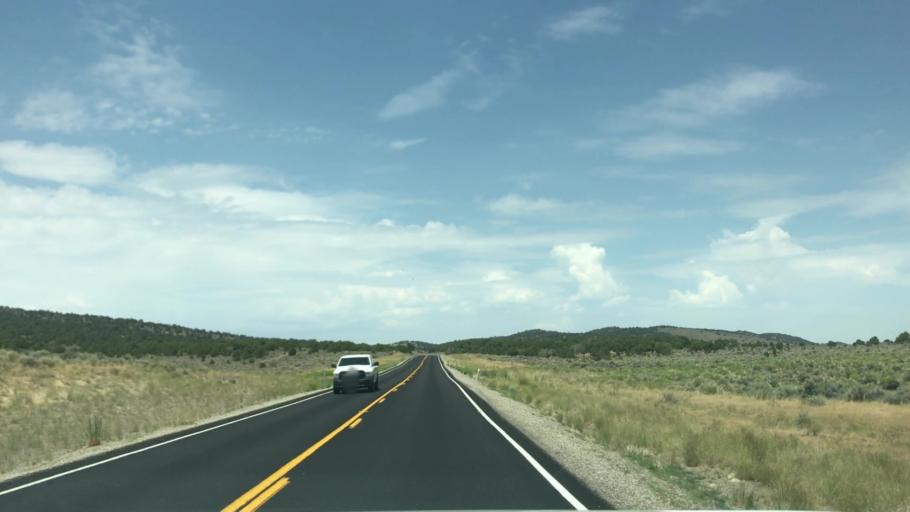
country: US
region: Nevada
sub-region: Eureka County
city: Eureka
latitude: 39.3895
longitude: -115.4504
